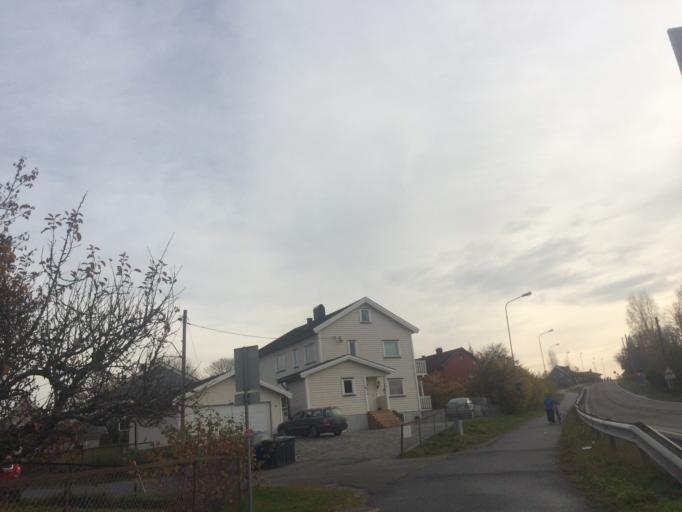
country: NO
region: Akershus
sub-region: Ski
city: Ski
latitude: 59.7239
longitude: 10.8439
